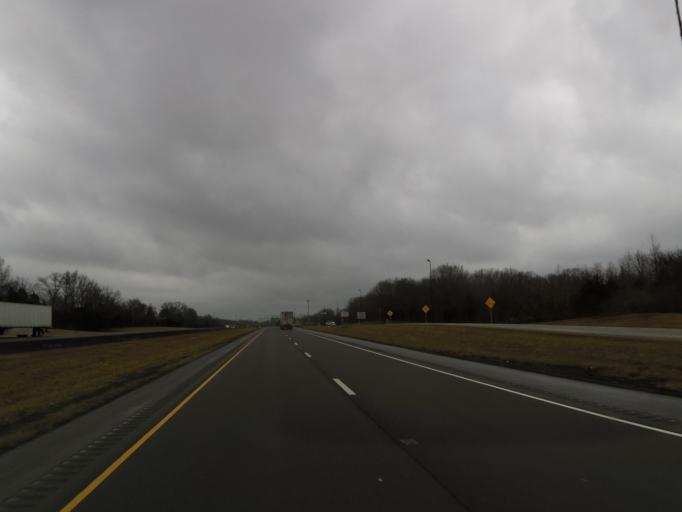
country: US
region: Illinois
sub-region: Johnson County
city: Goreville
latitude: 37.6460
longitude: -88.9770
